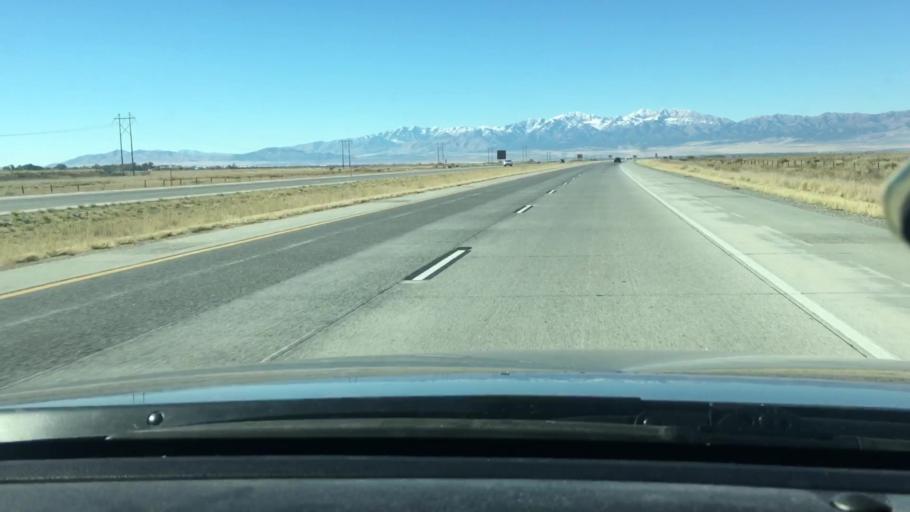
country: US
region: Utah
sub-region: Tooele County
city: Stansbury park
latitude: 40.6774
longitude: -112.2835
